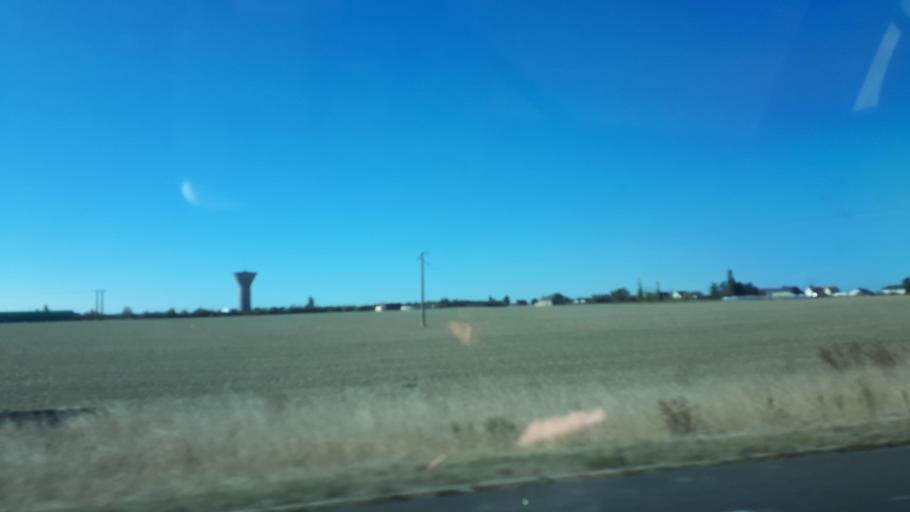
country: FR
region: Centre
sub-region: Departement d'Eure-et-Loir
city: Chateaudun
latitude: 48.0926
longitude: 1.3536
